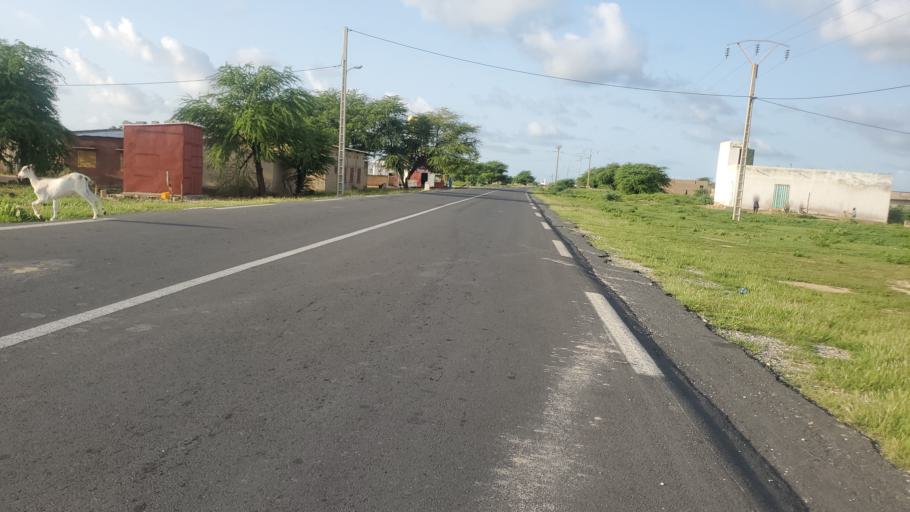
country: SN
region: Saint-Louis
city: Saint-Louis
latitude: 16.1348
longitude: -16.4116
